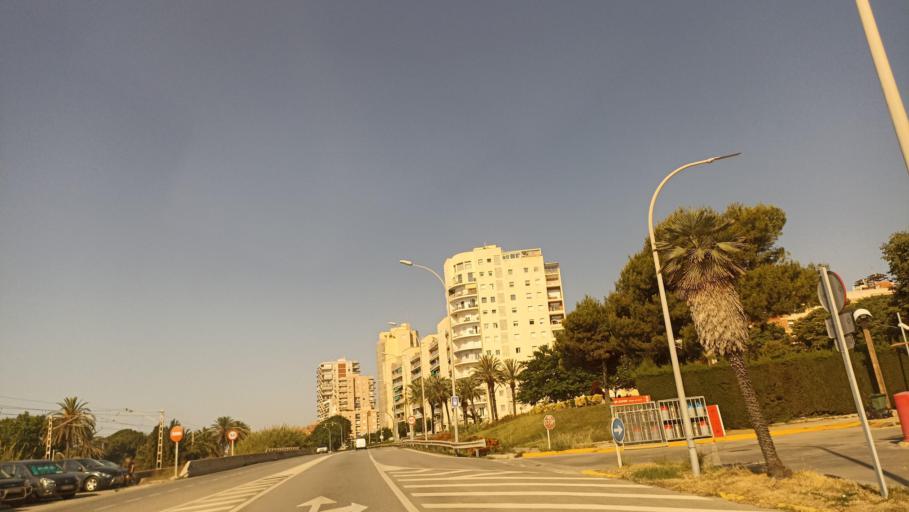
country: ES
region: Catalonia
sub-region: Provincia de Barcelona
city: Mataro
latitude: 41.5415
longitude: 2.4578
